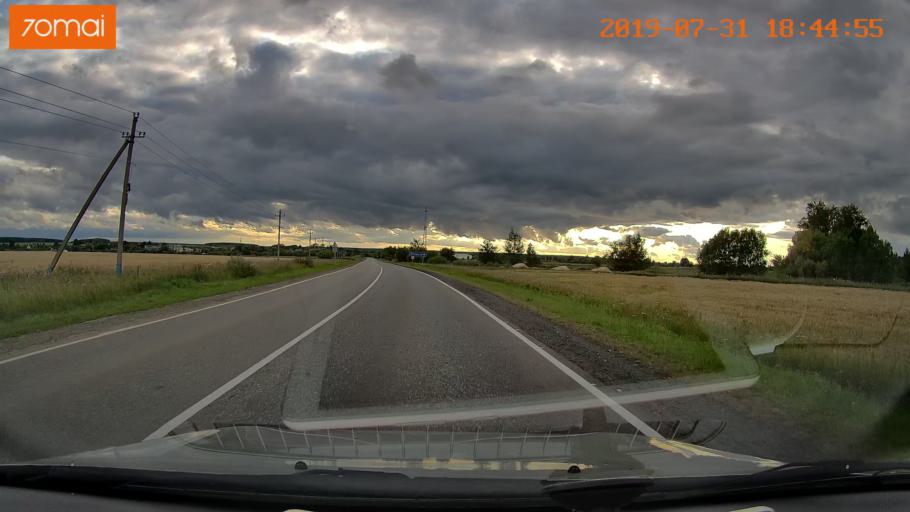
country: RU
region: Moskovskaya
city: Troitskoye
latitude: 55.2522
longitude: 38.5422
